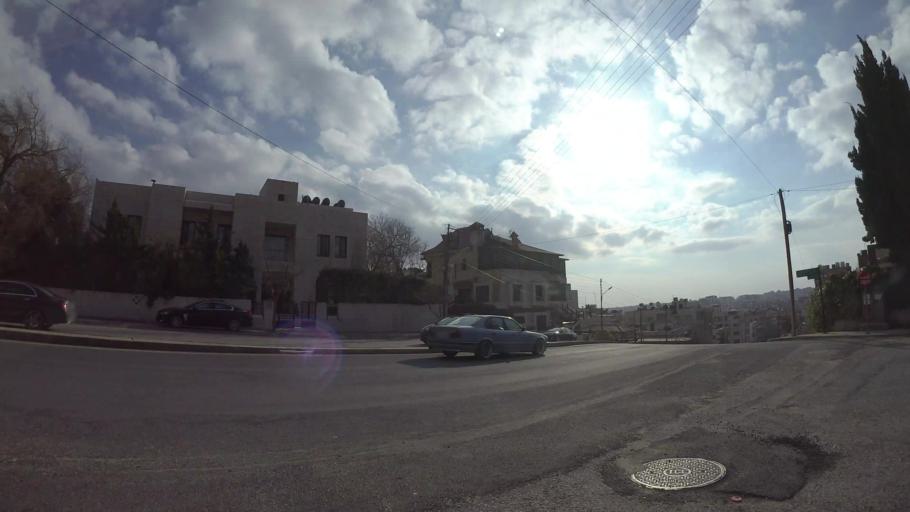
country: JO
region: Amman
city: Al Jubayhah
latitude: 31.9798
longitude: 35.8774
